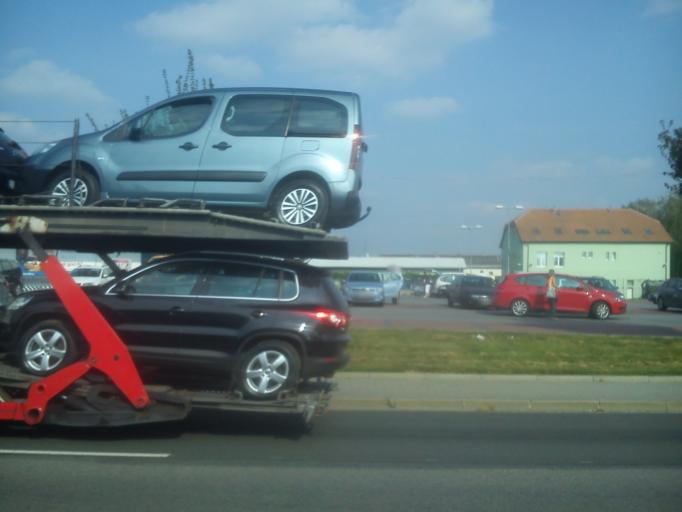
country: CZ
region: South Moravian
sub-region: Mesto Brno
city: Brno
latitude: 49.1711
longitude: 16.6253
